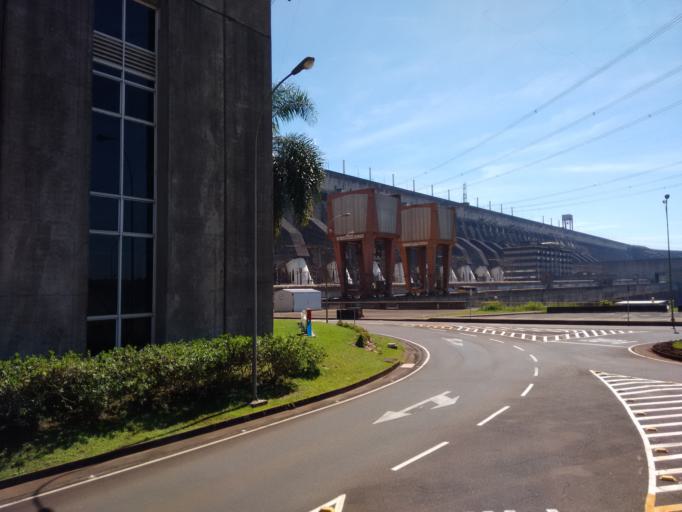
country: PY
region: Alto Parana
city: Ciudad del Este
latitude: -25.4086
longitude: -54.5939
